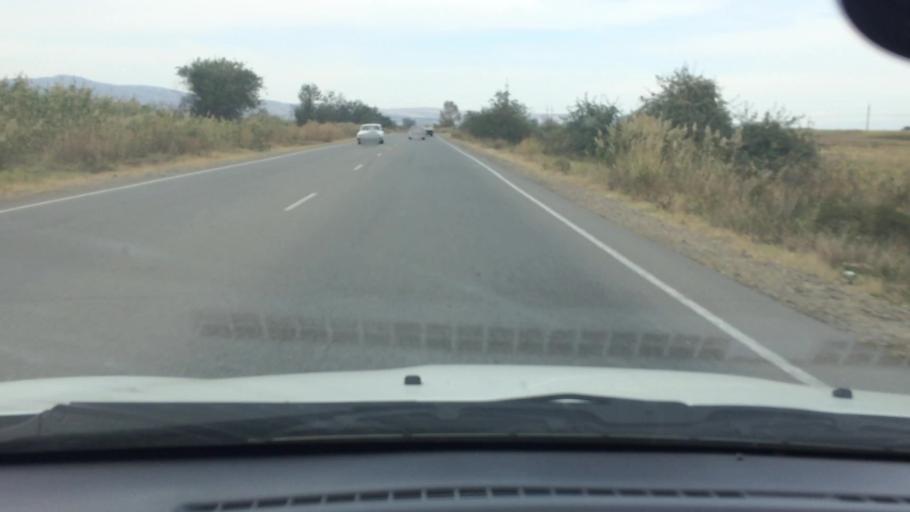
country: GE
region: Kvemo Kartli
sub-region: Marneuli
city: Marneuli
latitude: 41.5363
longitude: 44.7770
